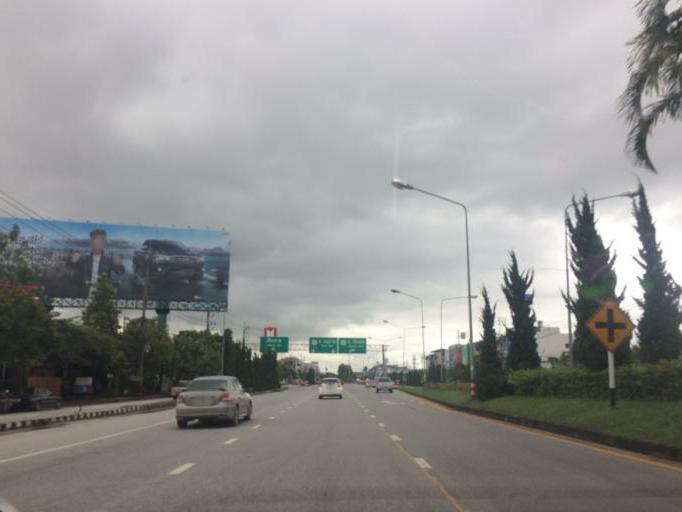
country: TH
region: Chiang Rai
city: Chiang Rai
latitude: 19.8956
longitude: 99.8382
